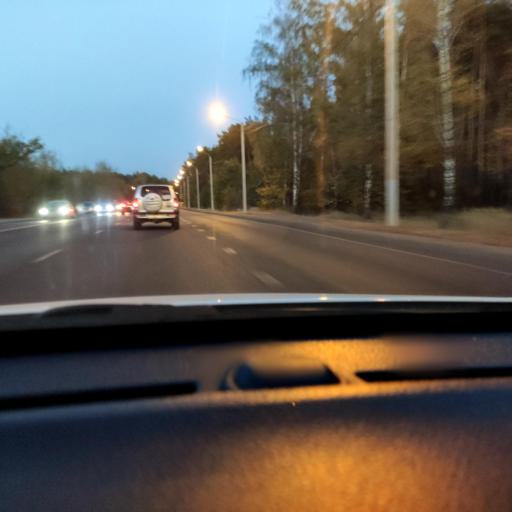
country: RU
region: Voronezj
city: Voronezh
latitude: 51.6806
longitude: 39.2749
